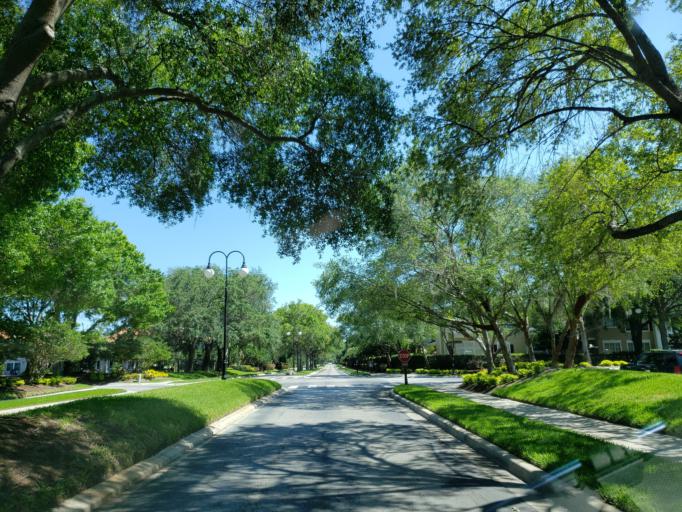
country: US
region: Florida
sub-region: Hillsborough County
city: Tampa
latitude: 27.9352
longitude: -82.4500
